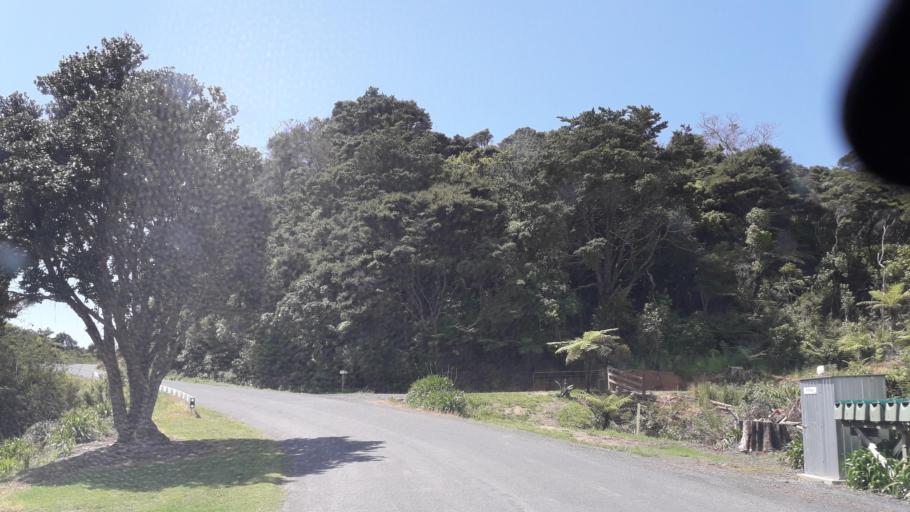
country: NZ
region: Northland
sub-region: Far North District
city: Paihia
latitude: -35.2358
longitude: 174.2605
